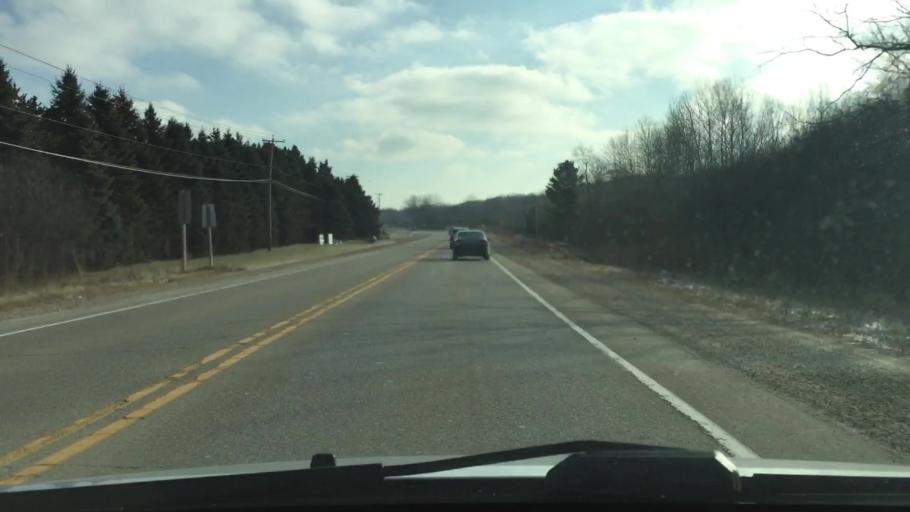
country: US
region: Wisconsin
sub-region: Waukesha County
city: Wales
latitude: 43.0137
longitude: -88.4009
